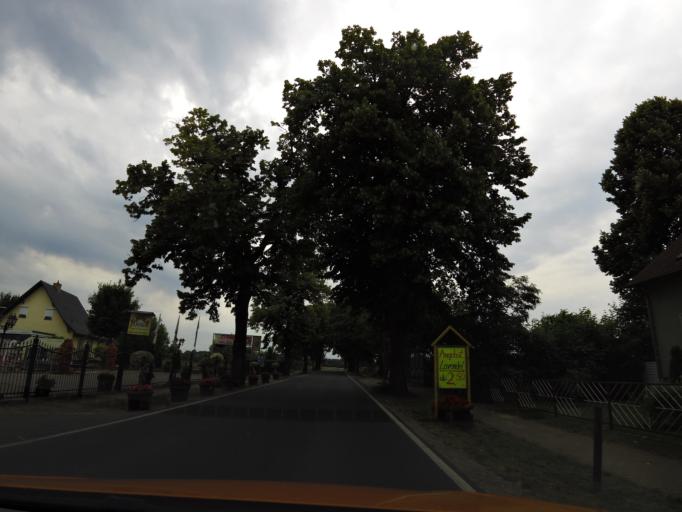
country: DE
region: Brandenburg
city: Zossen
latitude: 52.2234
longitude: 13.4231
